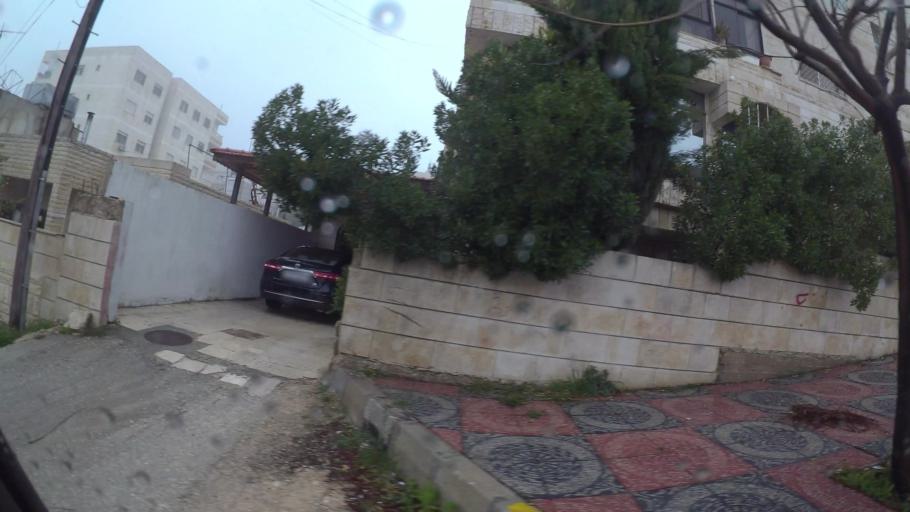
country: JO
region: Amman
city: Al Jubayhah
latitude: 32.0184
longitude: 35.8402
